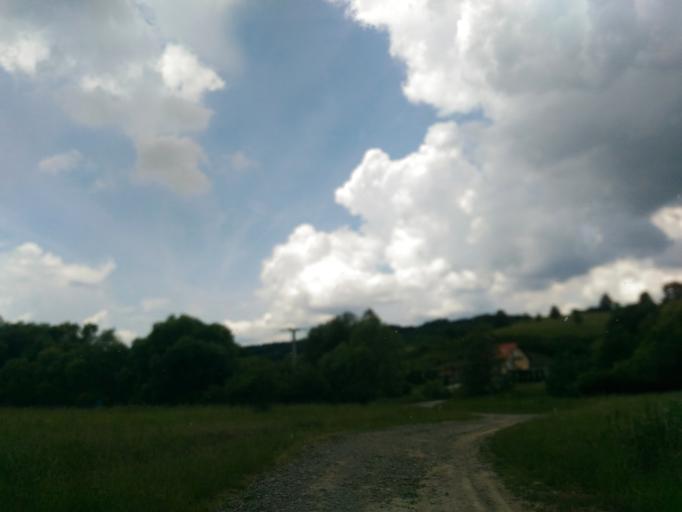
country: HU
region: Baranya
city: Komlo
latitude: 46.1588
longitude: 18.2260
